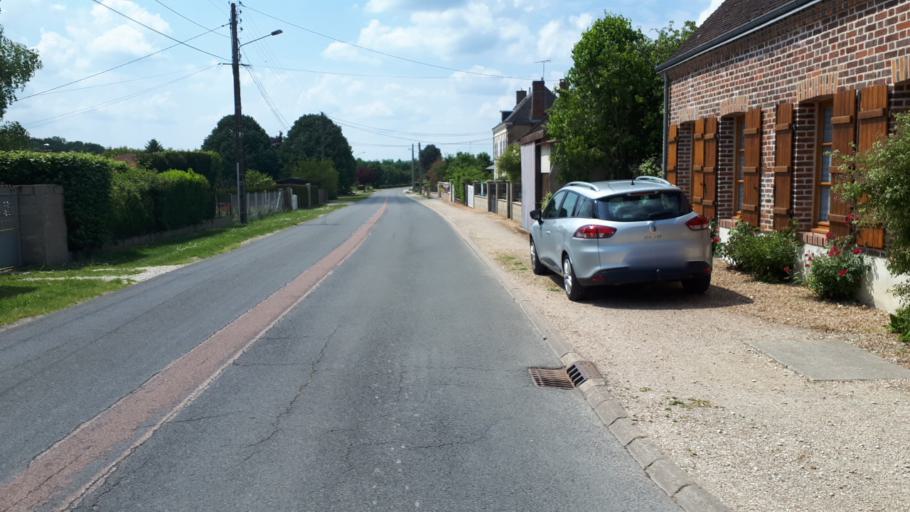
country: FR
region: Centre
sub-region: Departement du Loir-et-Cher
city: Aze
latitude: 47.8494
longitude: 0.9957
